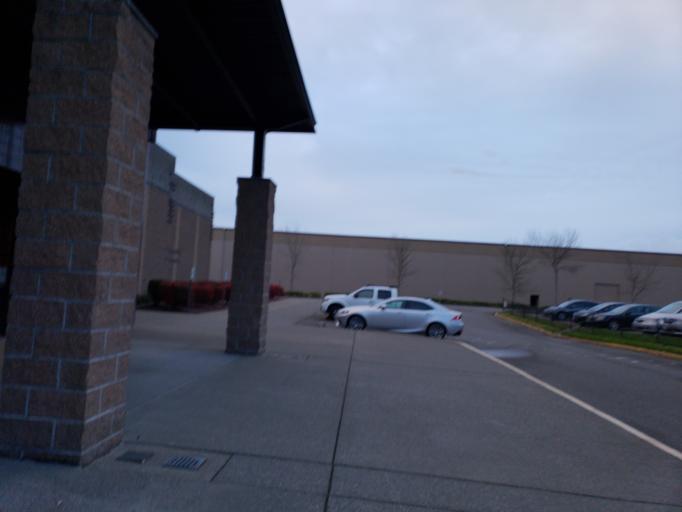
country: US
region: Washington
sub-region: King County
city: Tukwila
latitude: 47.4425
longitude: -122.2584
